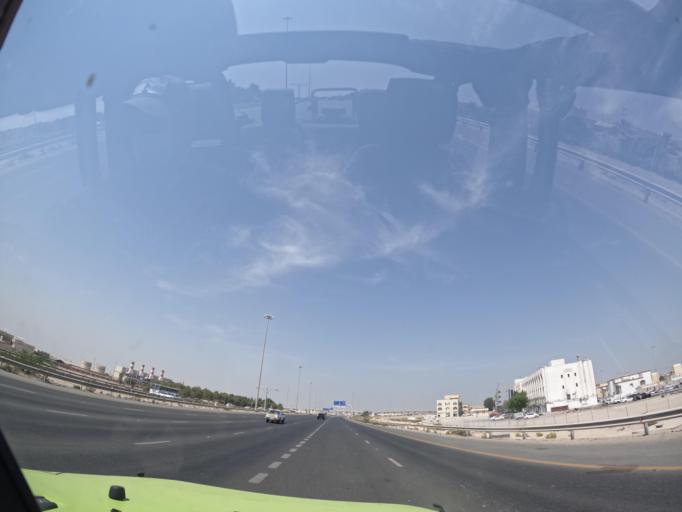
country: AE
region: Abu Dhabi
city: Abu Dhabi
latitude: 24.3046
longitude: 54.6140
